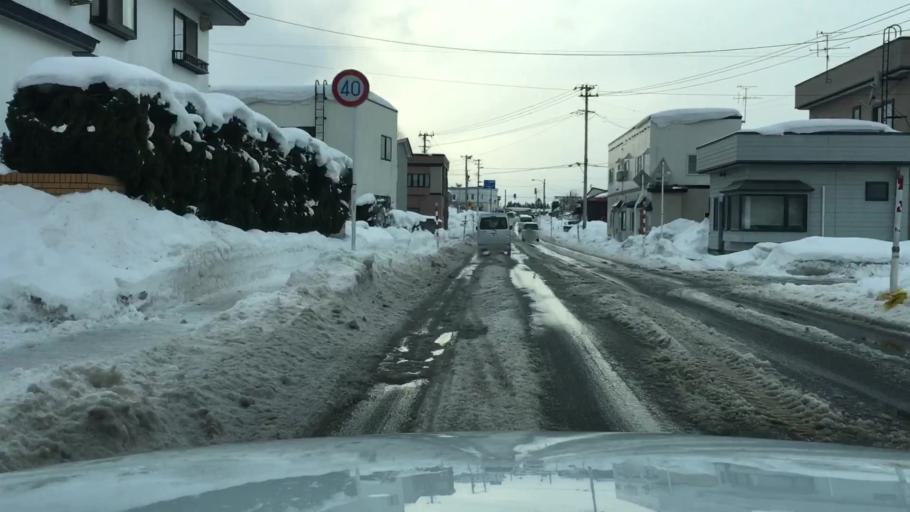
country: JP
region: Aomori
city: Kuroishi
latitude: 40.5915
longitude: 140.5594
